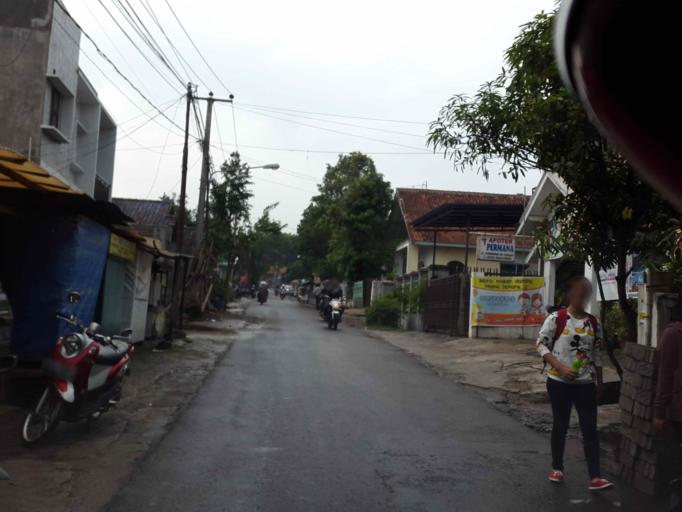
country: ID
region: West Java
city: Cimahi
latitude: -6.8621
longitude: 107.5524
